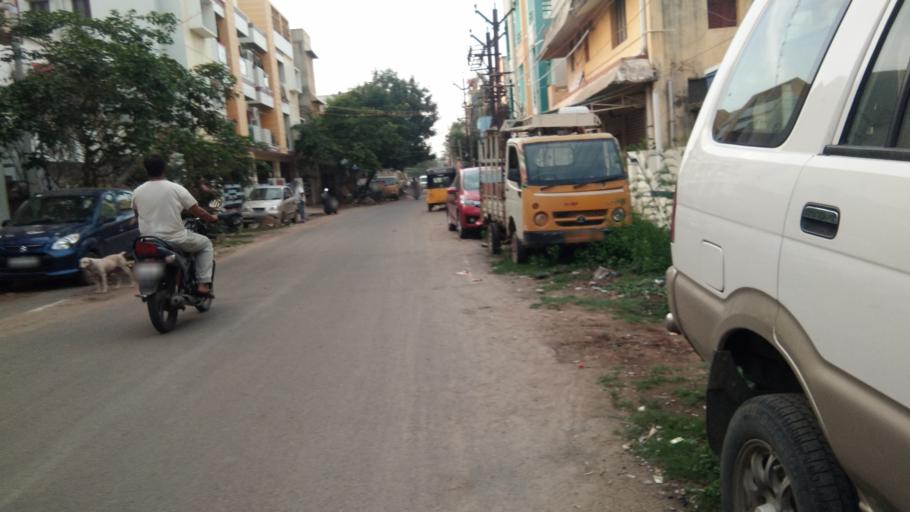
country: IN
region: Tamil Nadu
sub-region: Kancheepuram
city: Pallavaram
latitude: 12.9648
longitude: 80.1418
